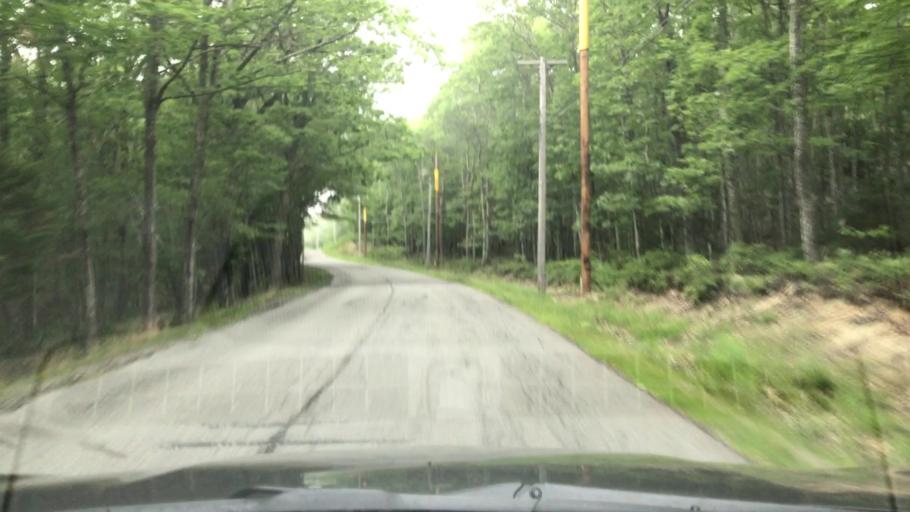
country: US
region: Maine
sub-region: Hancock County
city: Bar Harbor
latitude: 44.3477
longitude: -68.1816
